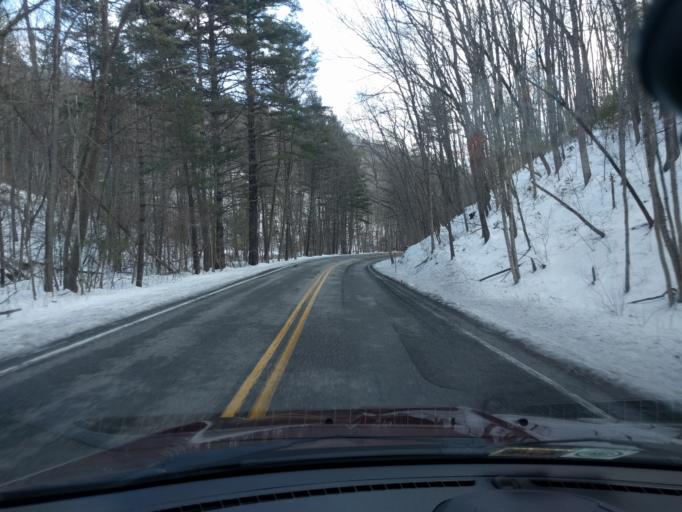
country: US
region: Virginia
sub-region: Bath County
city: Warm Springs
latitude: 38.1230
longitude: -79.9357
